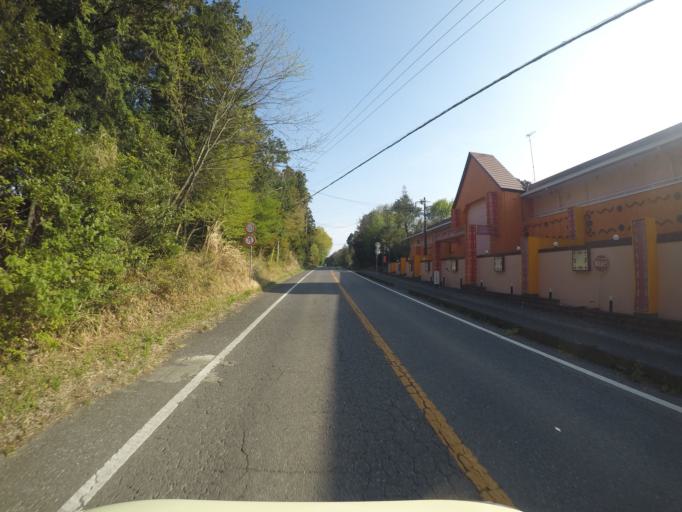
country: JP
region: Ibaraki
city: Ishige
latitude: 36.1790
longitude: 140.0181
